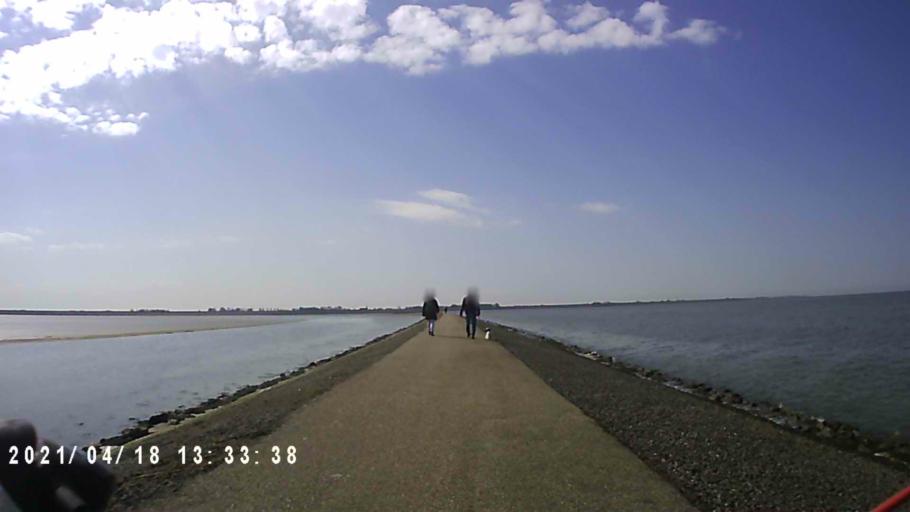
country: NL
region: Friesland
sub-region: Gemeente Dongeradeel
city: Anjum
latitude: 53.4133
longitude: 6.0976
